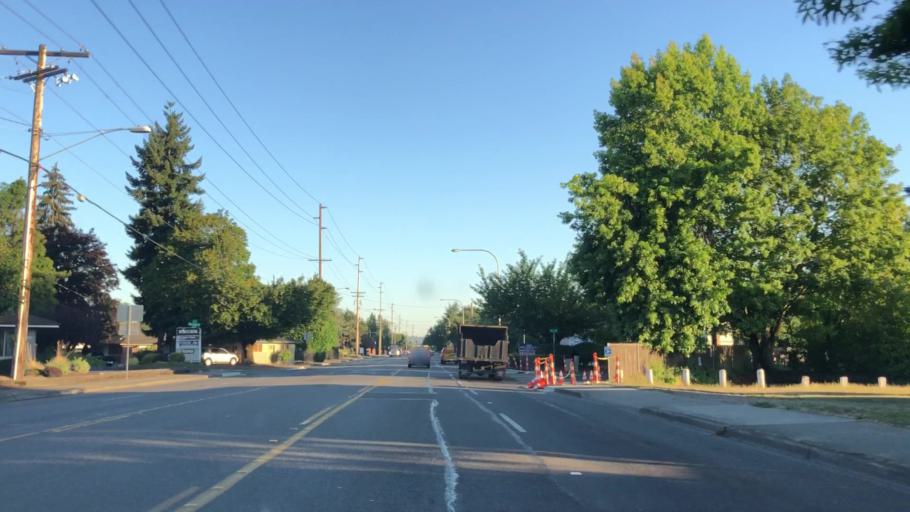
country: US
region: Washington
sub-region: King County
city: Auburn
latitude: 47.3165
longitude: -122.2157
